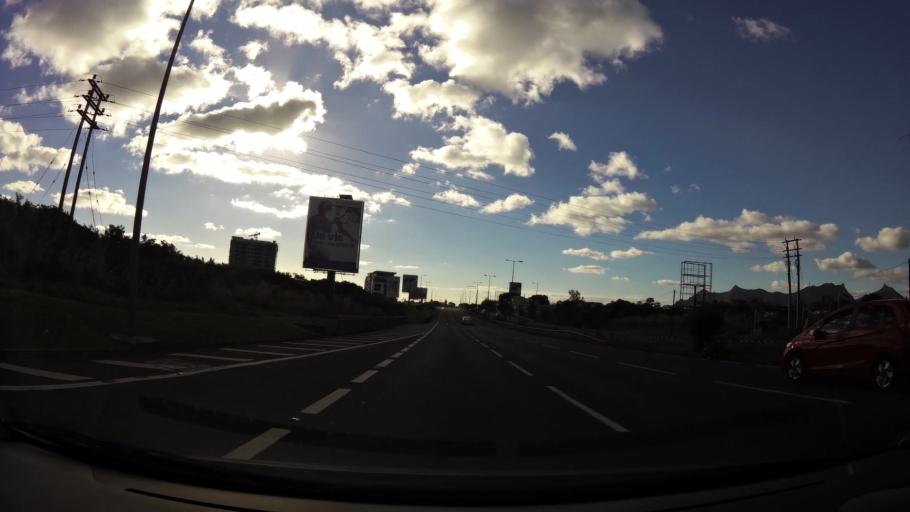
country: MU
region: Plaines Wilhems
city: Quatre Bornes
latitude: -20.2627
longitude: 57.4909
